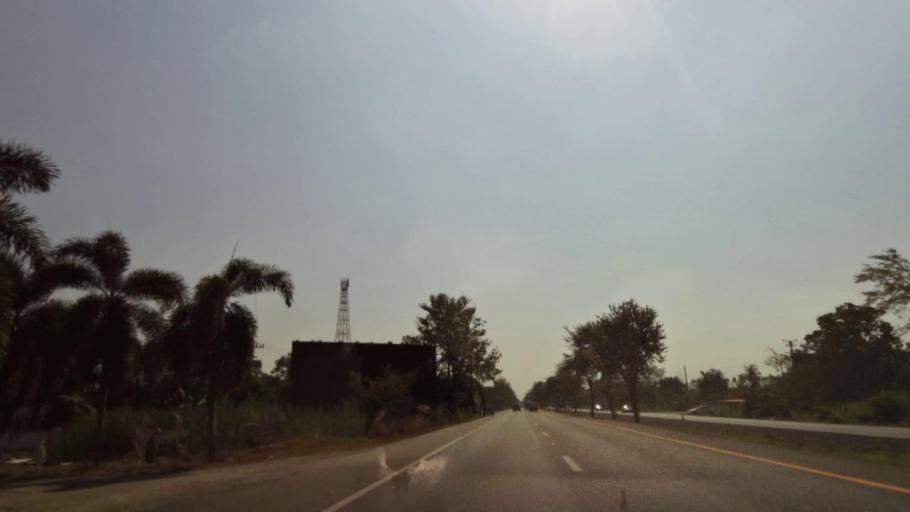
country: TH
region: Phichit
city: Bueng Na Rang
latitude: 16.0788
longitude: 100.1244
